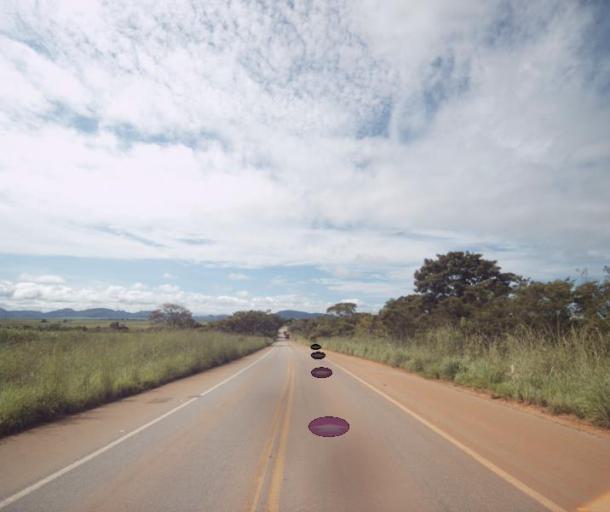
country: BR
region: Goias
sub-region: Barro Alto
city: Barro Alto
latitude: -15.0506
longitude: -48.8859
